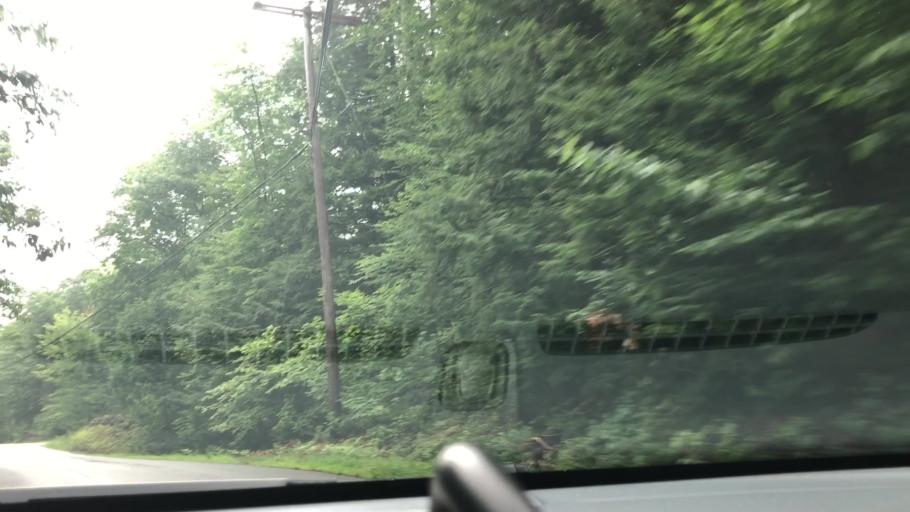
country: US
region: New Hampshire
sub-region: Hillsborough County
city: Pinardville
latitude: 42.9866
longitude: -71.5371
